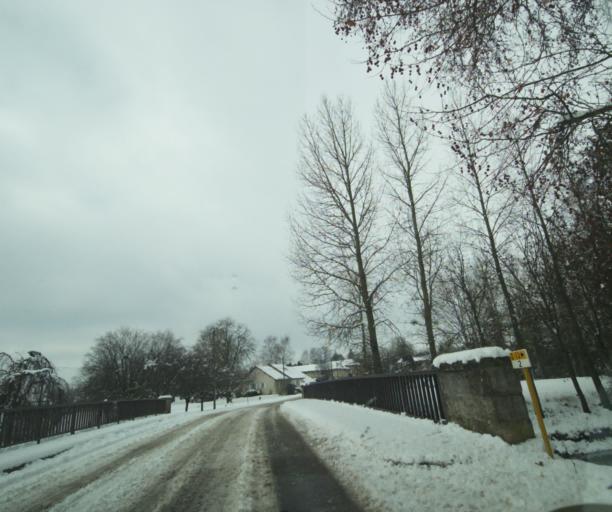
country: FR
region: Champagne-Ardenne
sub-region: Departement de la Haute-Marne
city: Montier-en-Der
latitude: 48.5109
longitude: 4.6971
